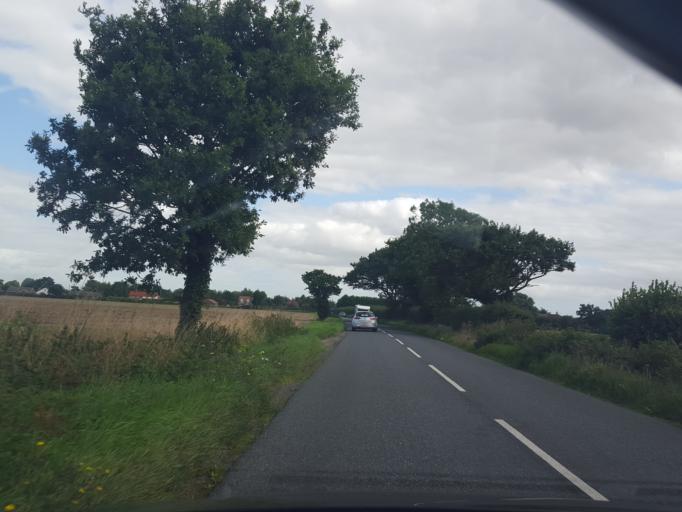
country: GB
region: England
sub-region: Essex
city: Mistley
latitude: 51.9252
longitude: 1.0924
